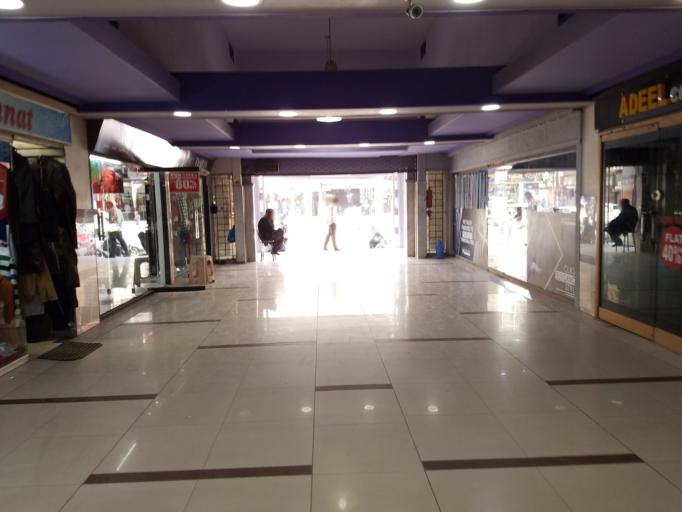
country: PK
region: Sindh
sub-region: Karachi District
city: Karachi
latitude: 24.8737
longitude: 67.0613
